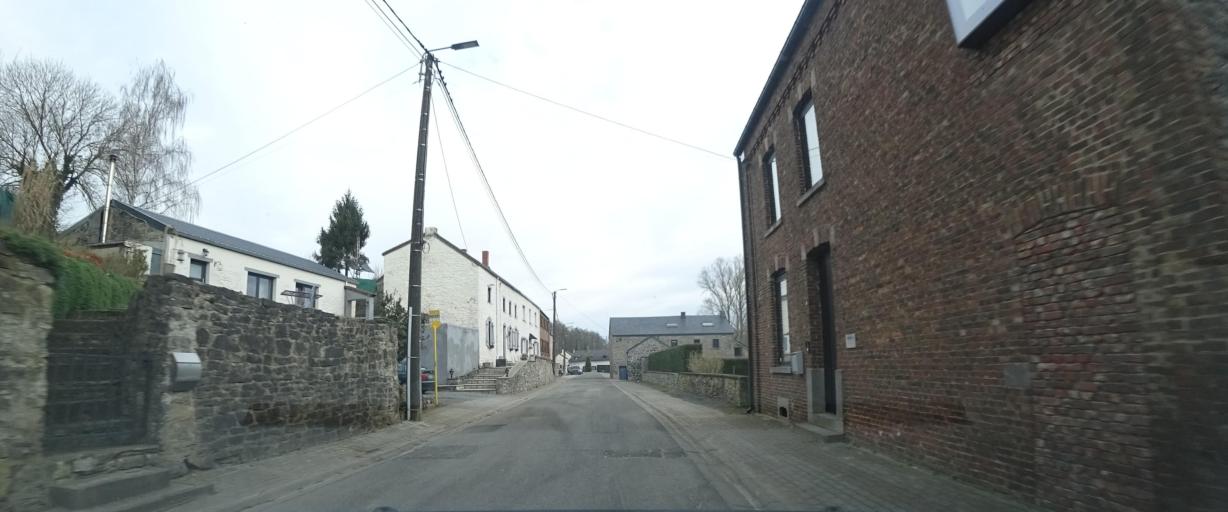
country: BE
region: Wallonia
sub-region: Province de Namur
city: Sombreffe
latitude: 50.5032
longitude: 4.6472
